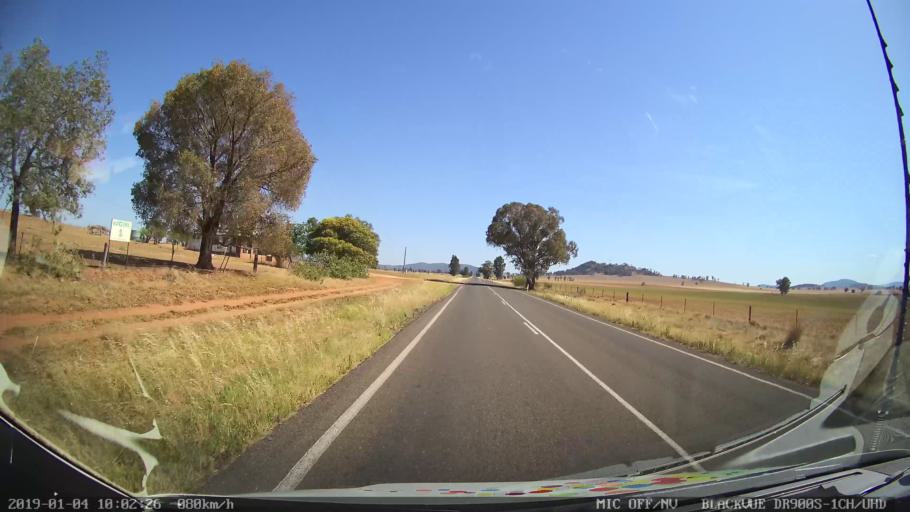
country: AU
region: New South Wales
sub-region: Cabonne
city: Canowindra
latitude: -33.4764
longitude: 148.3654
